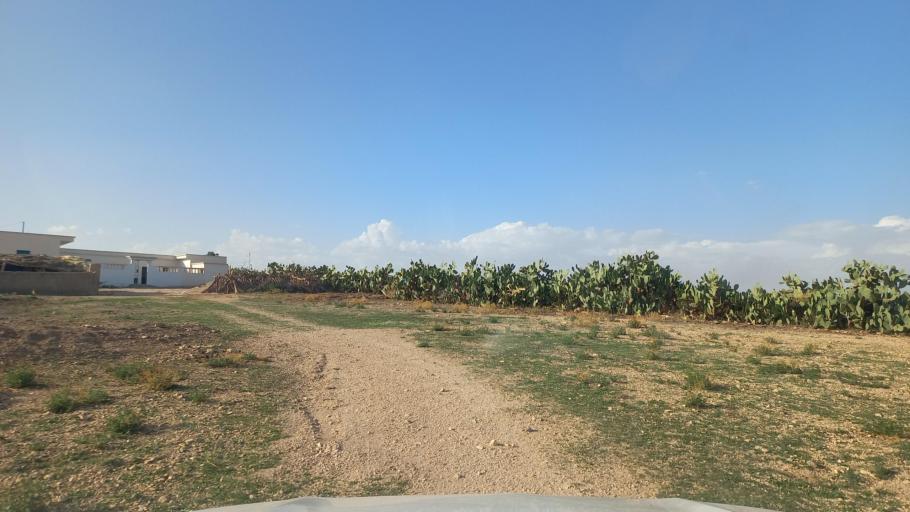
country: TN
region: Al Qasrayn
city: Sbiba
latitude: 35.3659
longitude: 9.0051
